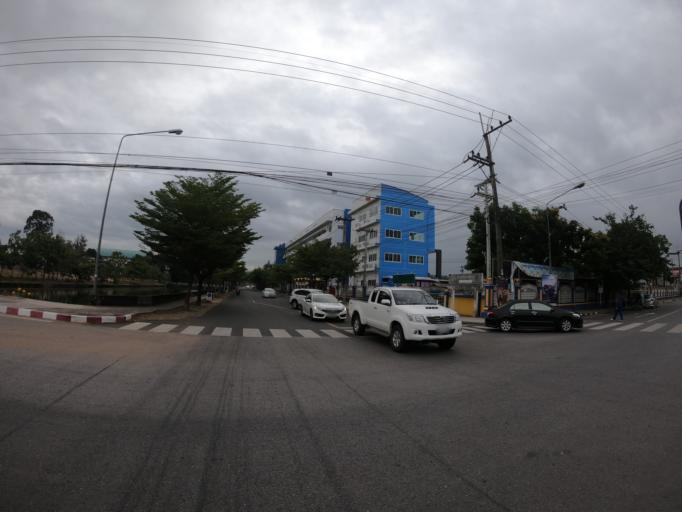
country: TH
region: Roi Et
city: Roi Et
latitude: 16.0498
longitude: 103.6539
